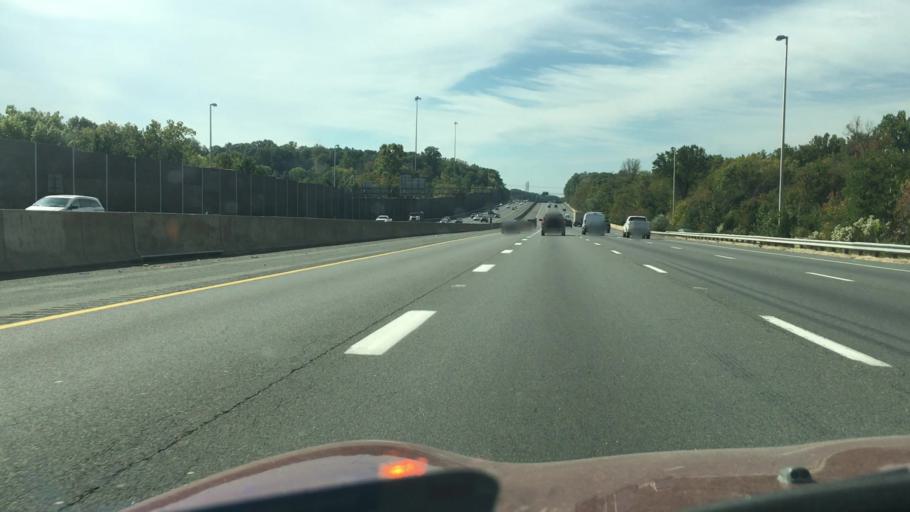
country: US
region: Virginia
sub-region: Fairfax County
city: Centreville
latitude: 38.8358
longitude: -77.4484
